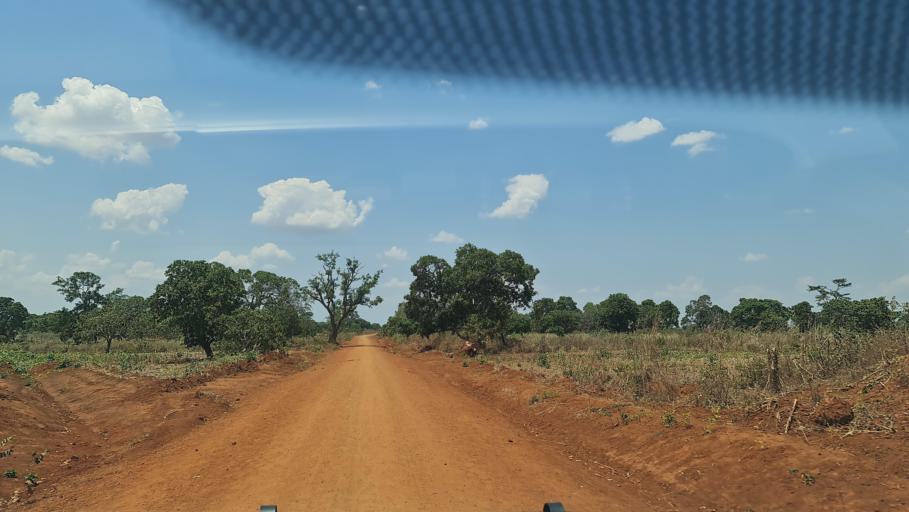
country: MZ
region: Nampula
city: Nacala
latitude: -14.7892
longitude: 40.0646
